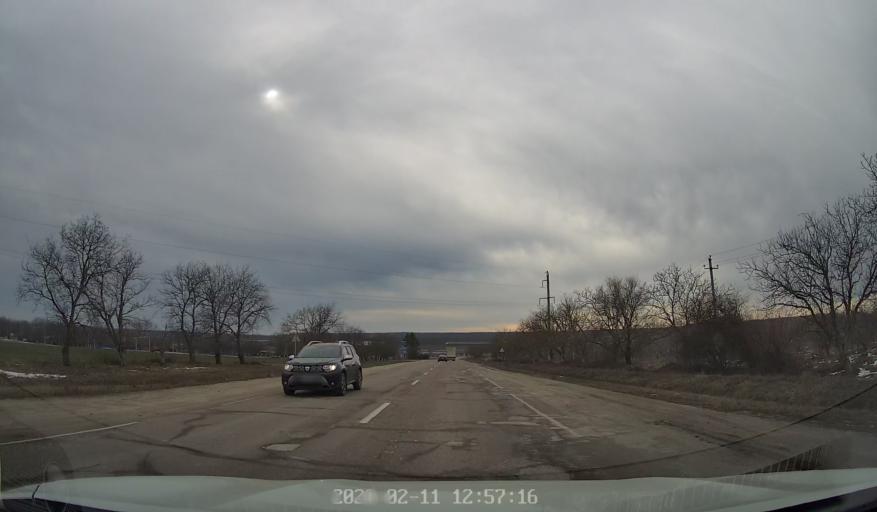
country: MD
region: Briceni
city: Briceni
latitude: 48.3426
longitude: 27.0686
